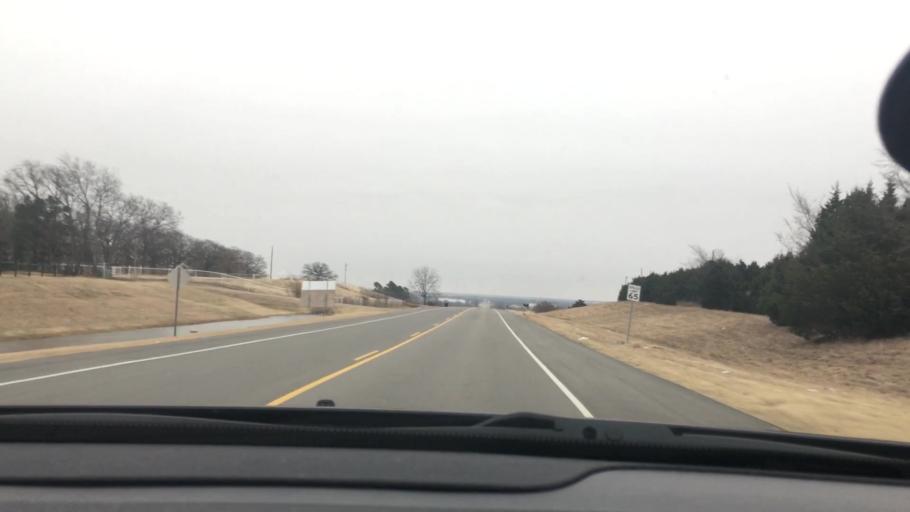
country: US
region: Oklahoma
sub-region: Garvin County
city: Wynnewood
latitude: 34.6227
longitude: -97.2115
